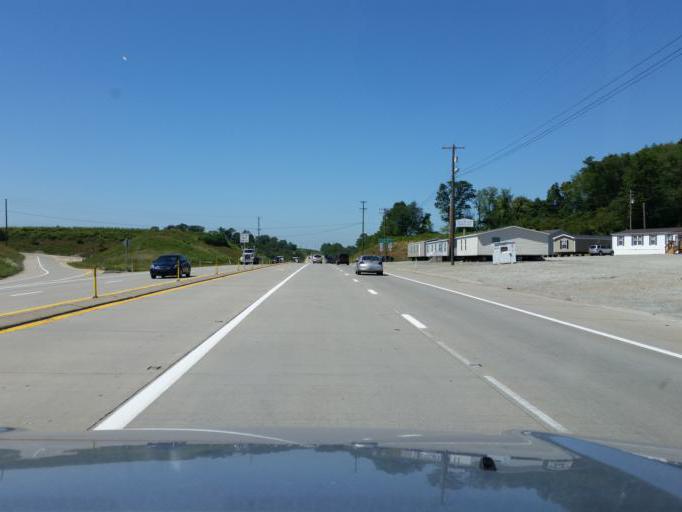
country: US
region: Pennsylvania
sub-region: Westmoreland County
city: Loyalhanna
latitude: 40.4181
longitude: -79.3684
